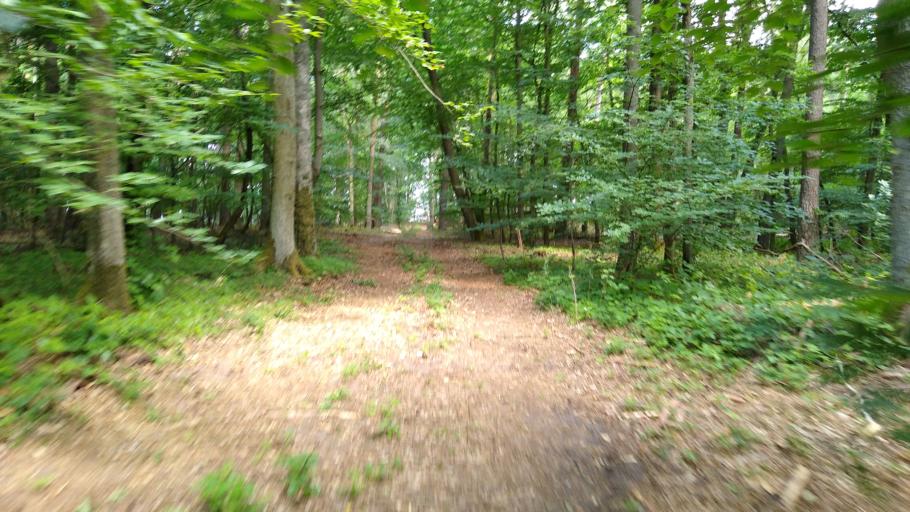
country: DE
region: Bavaria
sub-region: Regierungsbezirk Mittelfranken
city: Seukendorf
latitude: 49.4867
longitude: 10.9048
